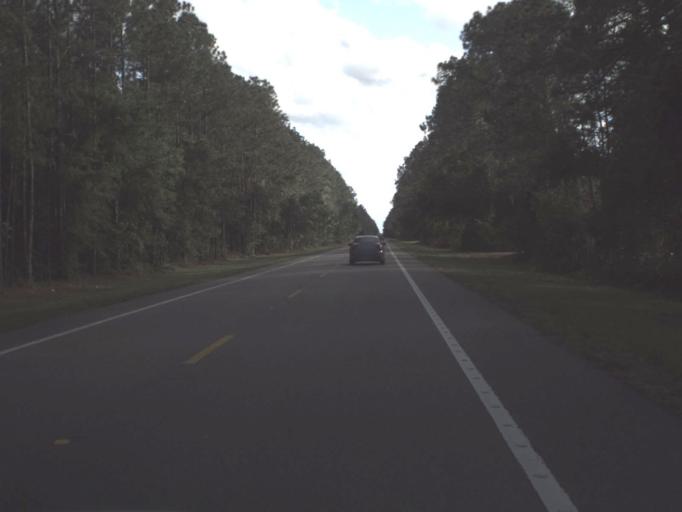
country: US
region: Florida
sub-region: Flagler County
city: Bunnell
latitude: 29.3105
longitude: -81.3153
